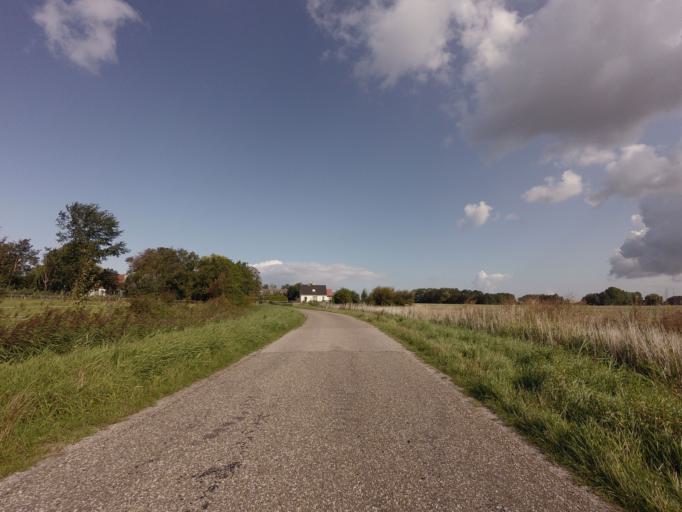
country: NL
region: Friesland
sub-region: Gemeente Franekeradeel
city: Tzummarum
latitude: 53.2414
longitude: 5.5421
